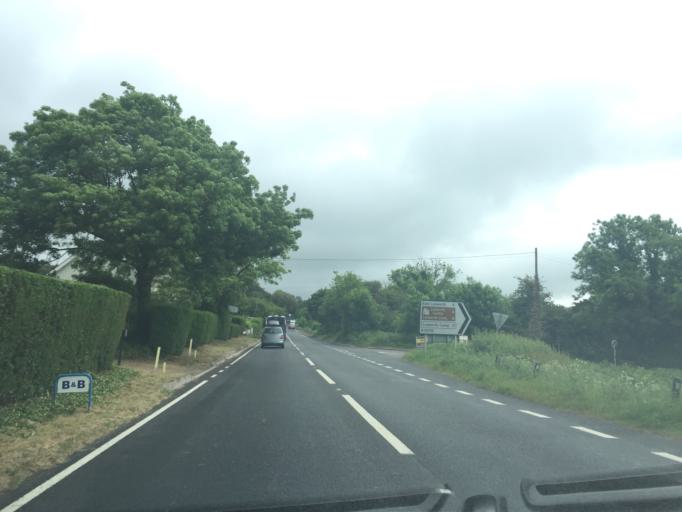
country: GB
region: England
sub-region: Dorset
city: Wareham
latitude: 50.6826
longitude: -2.1562
